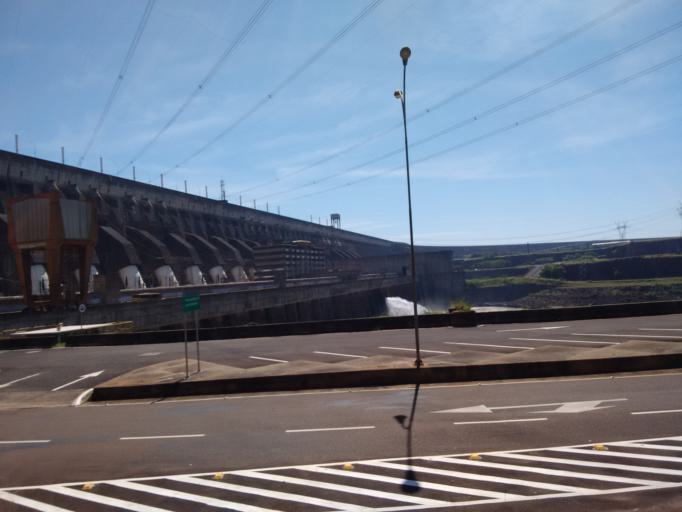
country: PY
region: Alto Parana
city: Ciudad del Este
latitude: -25.4089
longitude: -54.5935
